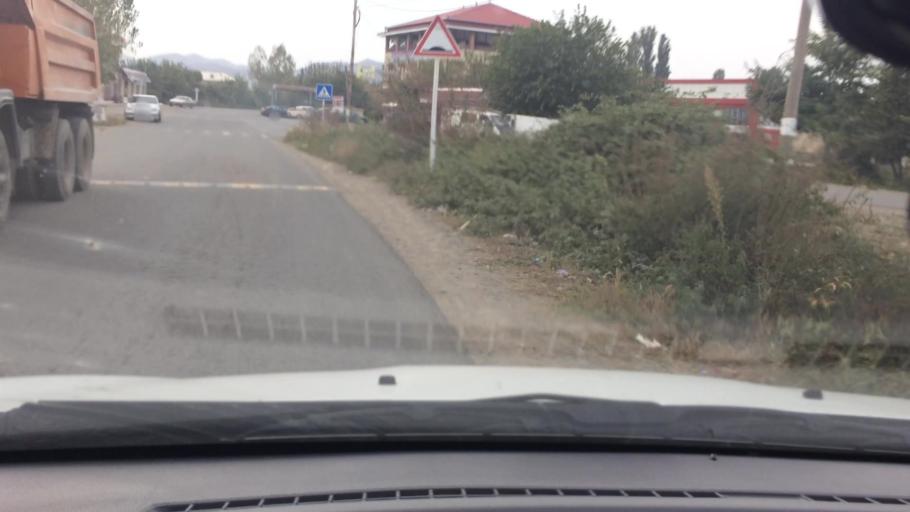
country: GE
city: Naghvarevi
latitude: 41.3541
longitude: 44.8618
